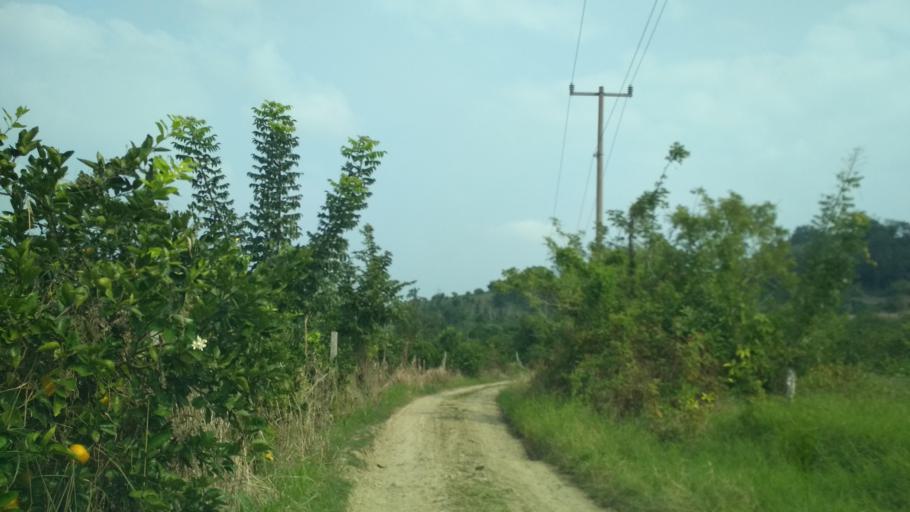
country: MM
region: Kayah
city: Loikaw
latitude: 20.2074
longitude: 97.3166
